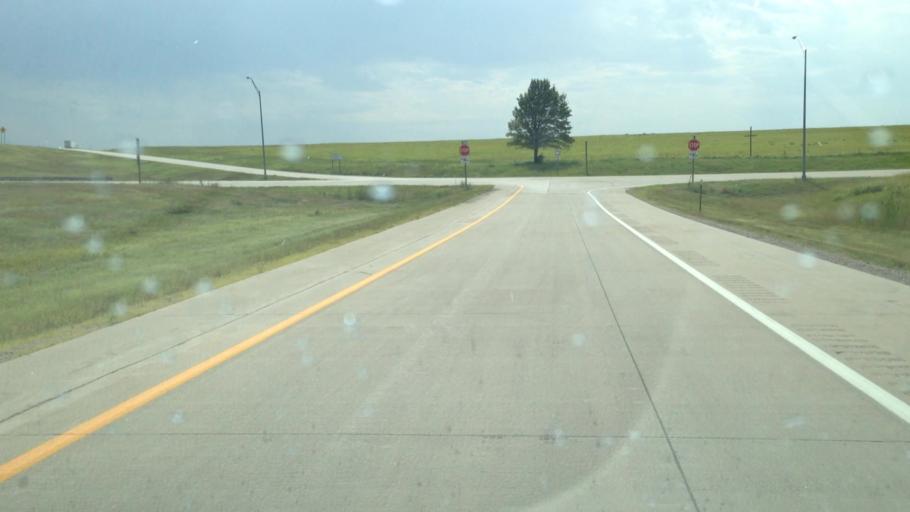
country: US
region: Kansas
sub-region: Osage County
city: Lyndon
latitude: 38.4302
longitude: -95.7274
